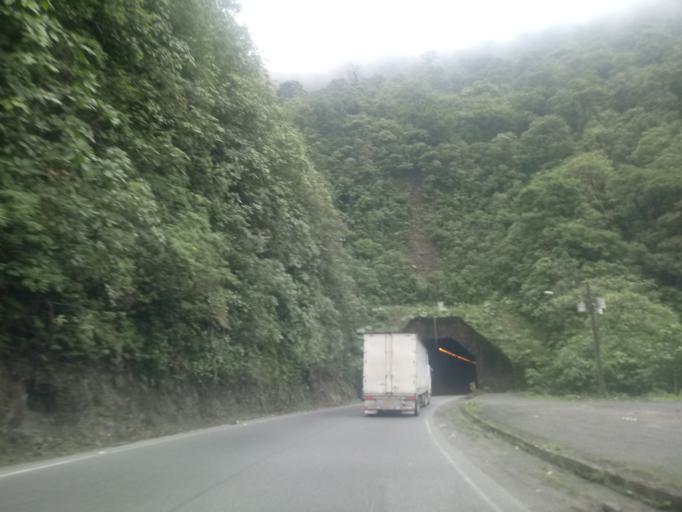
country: CR
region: Heredia
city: Angeles
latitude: 10.0604
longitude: -84.0081
